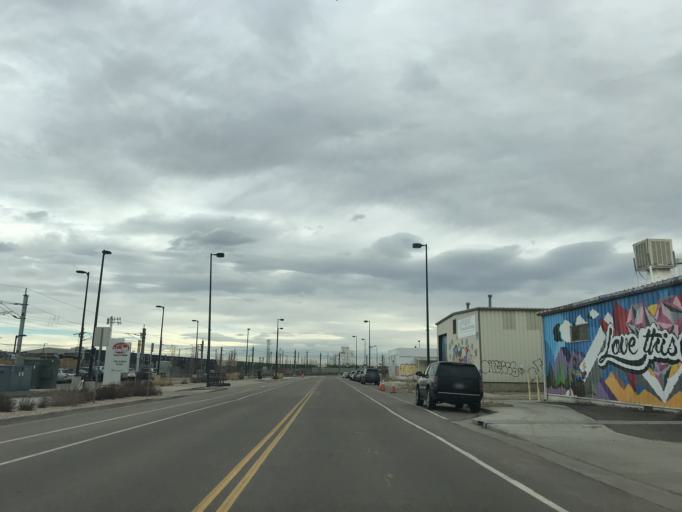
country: US
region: Colorado
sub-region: Denver County
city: Denver
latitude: 39.7714
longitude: -104.9722
